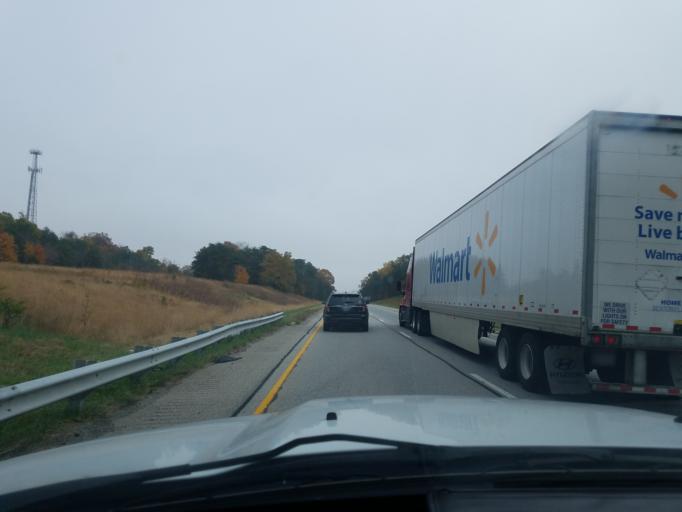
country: US
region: Indiana
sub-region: Floyd County
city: Georgetown
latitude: 38.2770
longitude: -85.9551
